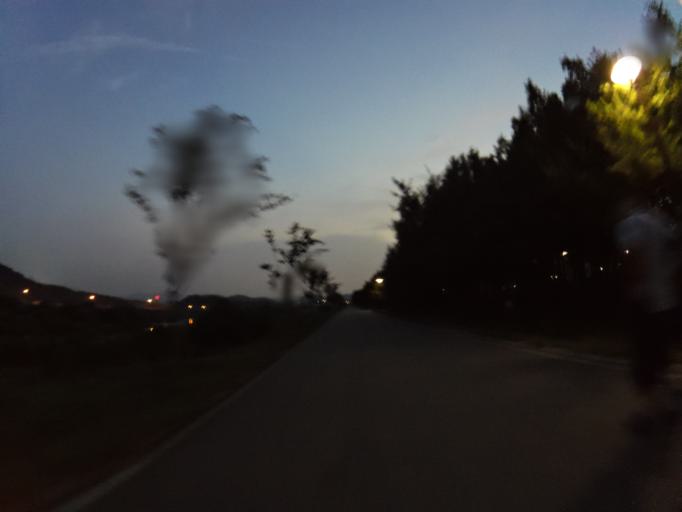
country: KR
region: Gyeongsangbuk-do
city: Gyeongsan-si
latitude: 35.8588
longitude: 128.6978
